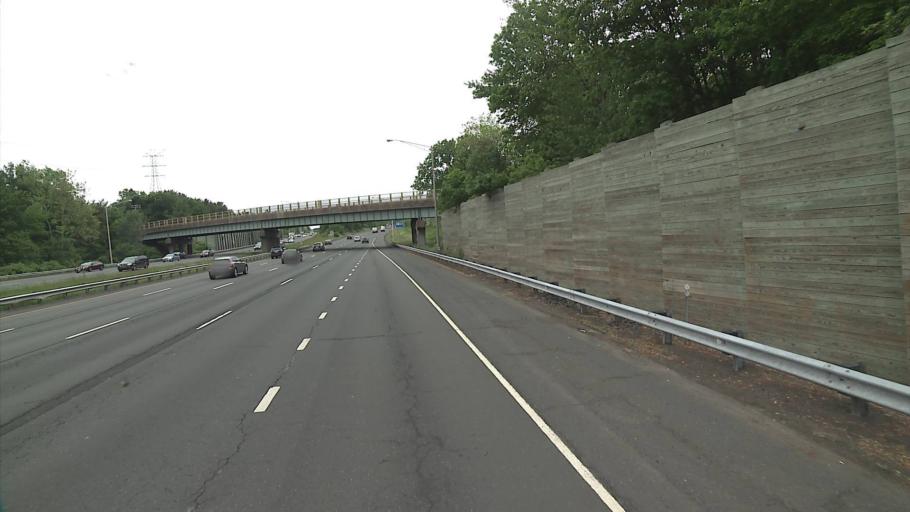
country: US
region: Connecticut
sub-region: Hartford County
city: Wethersfield
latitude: 41.6762
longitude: -72.6582
